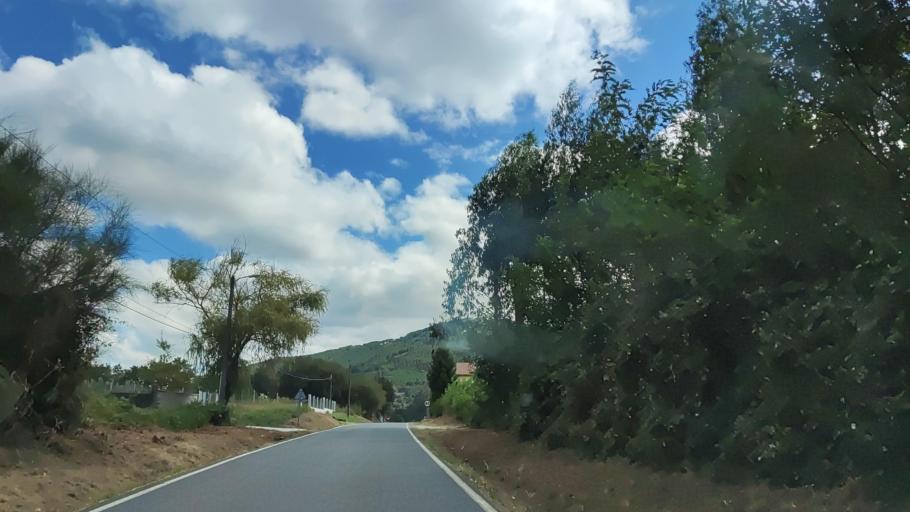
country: ES
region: Galicia
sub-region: Provincia da Coruna
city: Padron
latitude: 42.7832
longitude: -8.6590
